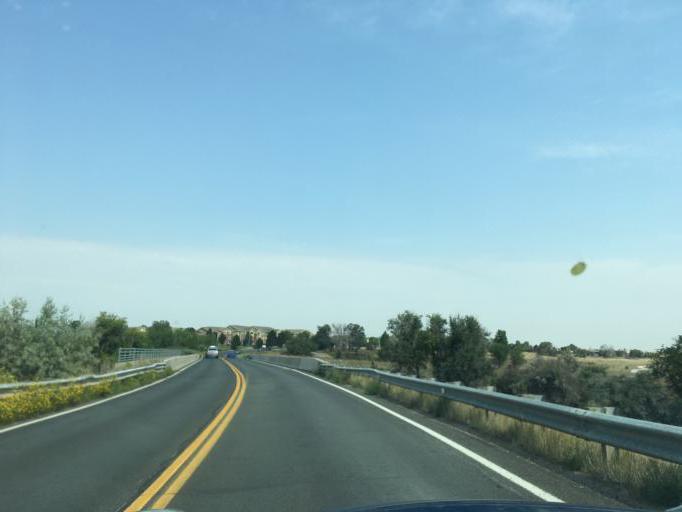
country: US
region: Colorado
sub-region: Adams County
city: Northglenn
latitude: 39.9224
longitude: -105.0139
